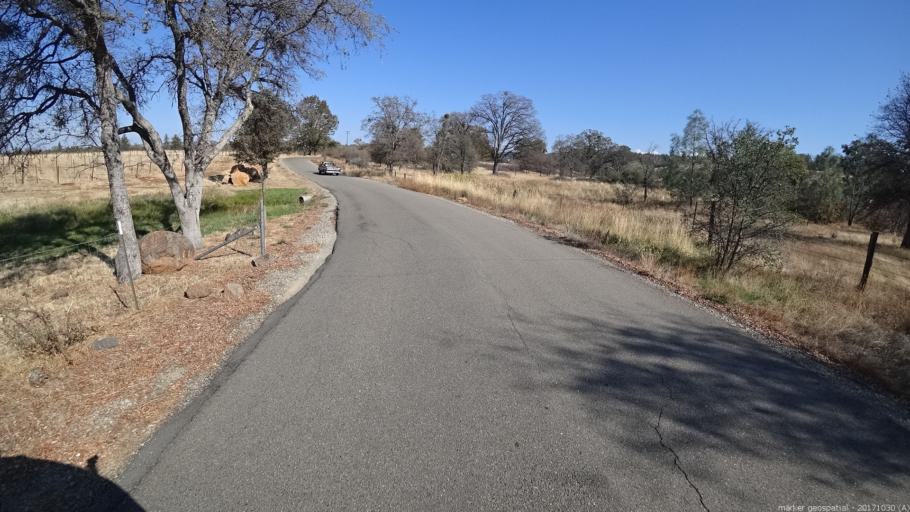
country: US
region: California
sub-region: Shasta County
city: Shingletown
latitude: 40.5088
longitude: -121.9954
